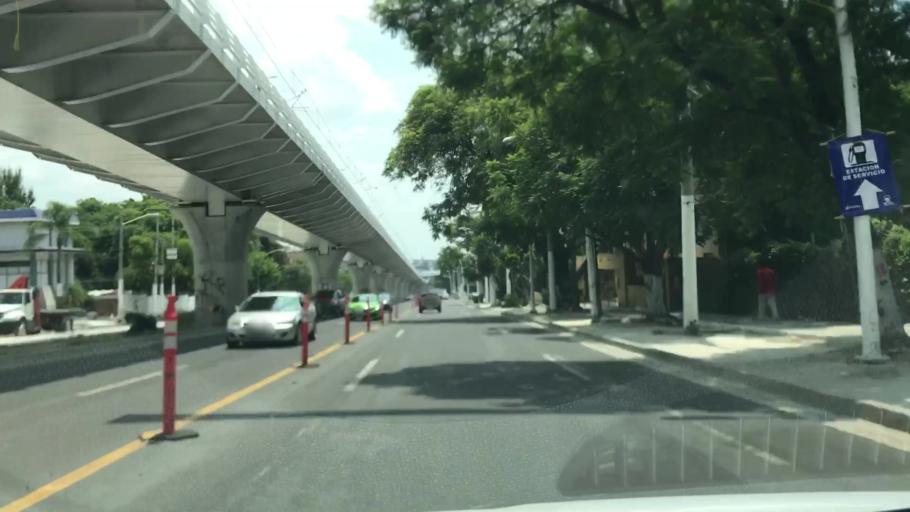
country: MX
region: Jalisco
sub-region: Zapopan
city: Zapopan
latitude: 20.7190
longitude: -103.3856
